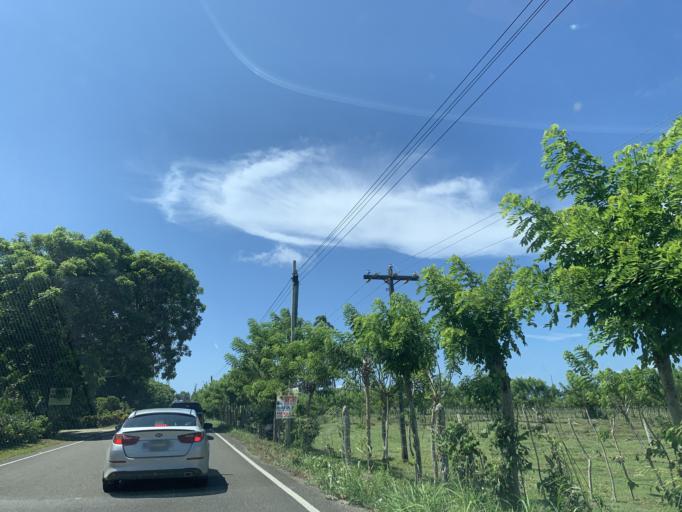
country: DO
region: Maria Trinidad Sanchez
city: Cabrera
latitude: 19.6682
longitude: -69.9503
